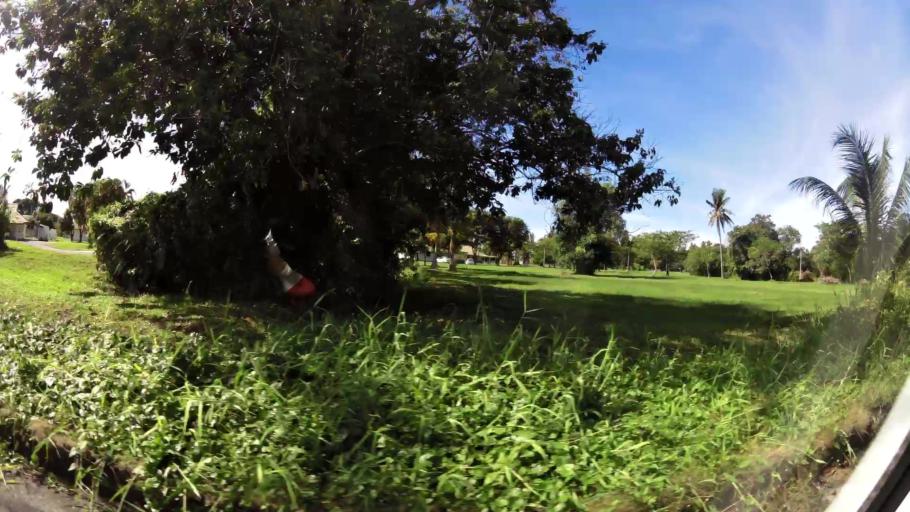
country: BN
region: Belait
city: Kuala Belait
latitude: 4.5866
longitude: 114.1983
